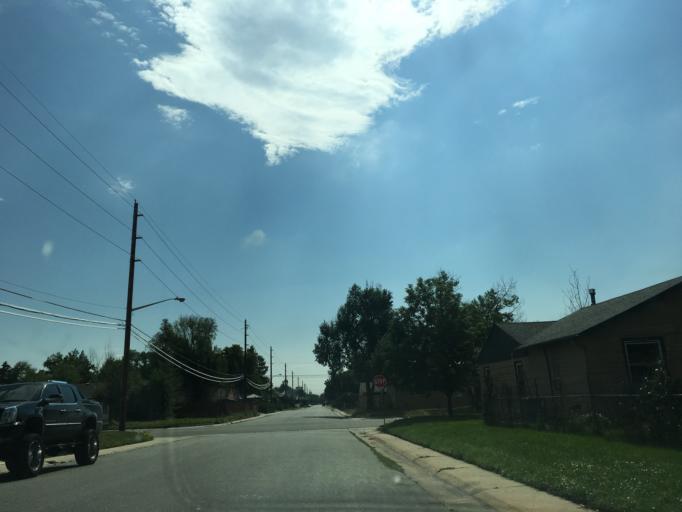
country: US
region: Colorado
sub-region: Jefferson County
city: Lakewood
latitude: 39.6949
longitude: -105.0467
